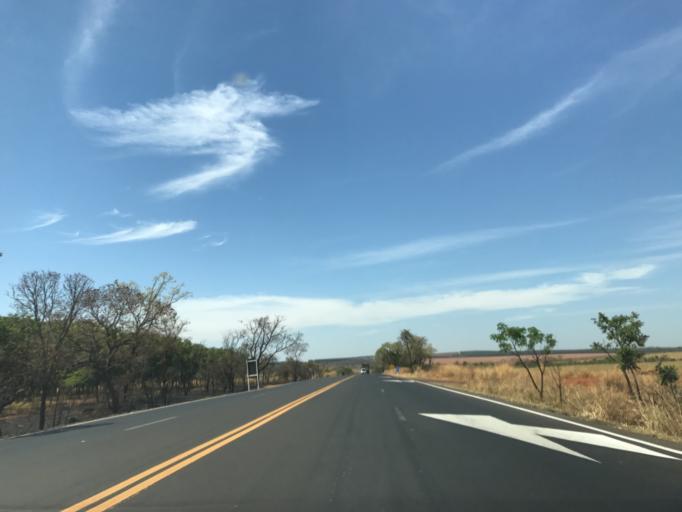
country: BR
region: Minas Gerais
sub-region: Monte Alegre De Minas
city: Monte Alegre de Minas
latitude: -19.0738
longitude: -49.0017
